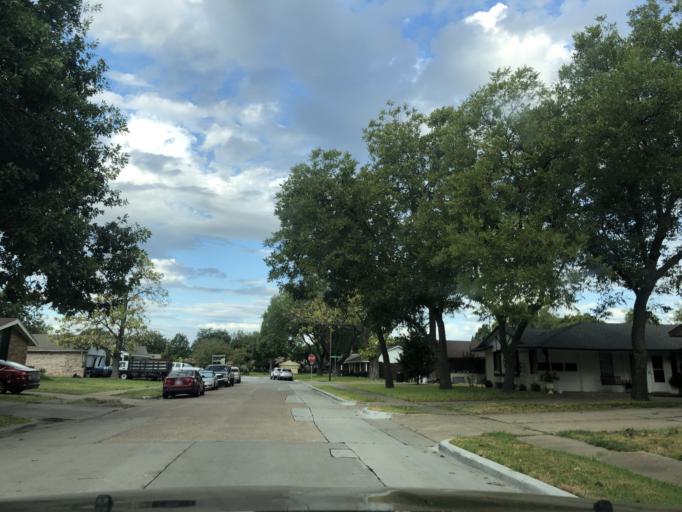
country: US
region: Texas
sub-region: Dallas County
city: Garland
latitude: 32.8737
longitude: -96.6516
